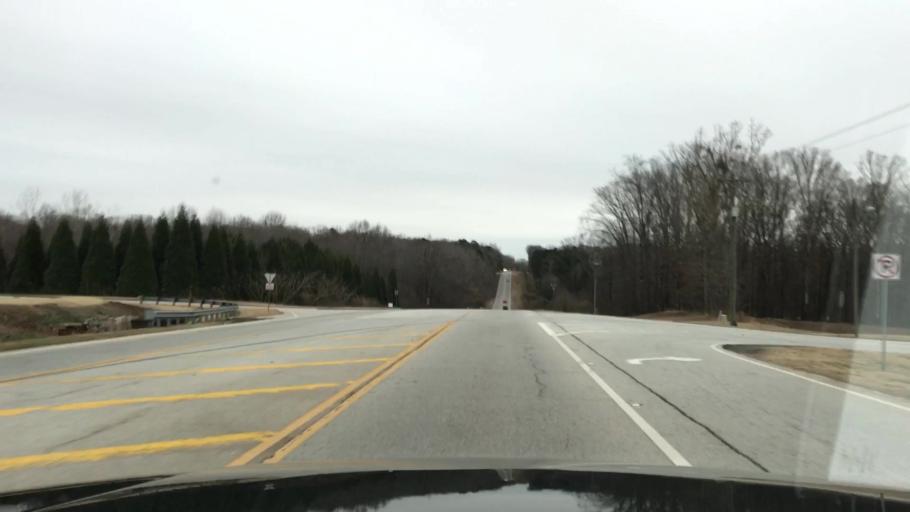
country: US
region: Georgia
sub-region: Walton County
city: Monroe
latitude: 33.8067
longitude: -83.6752
